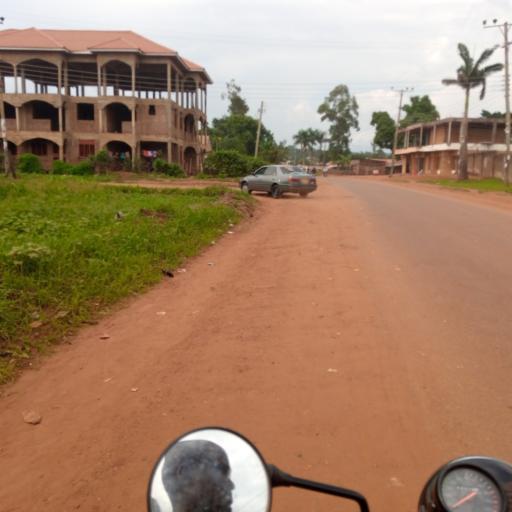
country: UG
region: Eastern Region
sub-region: Mbale District
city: Mbale
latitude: 1.0859
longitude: 34.1813
